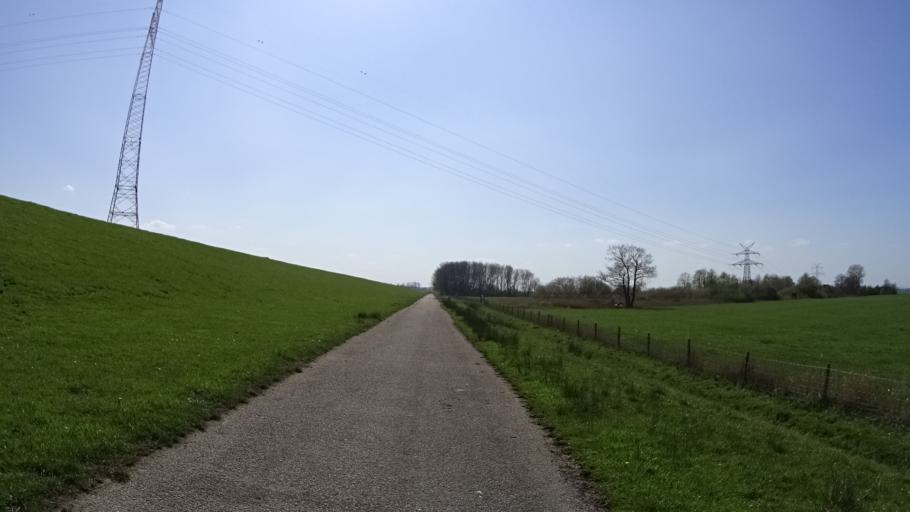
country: DE
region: Lower Saxony
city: Weener
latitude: 53.1493
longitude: 7.3706
